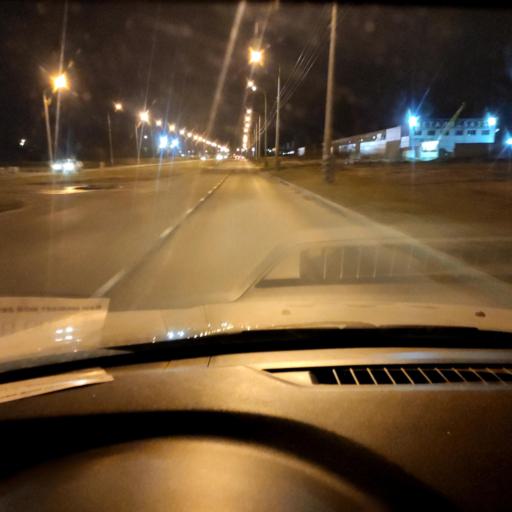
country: RU
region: Samara
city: Tol'yatti
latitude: 53.5573
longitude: 49.3328
